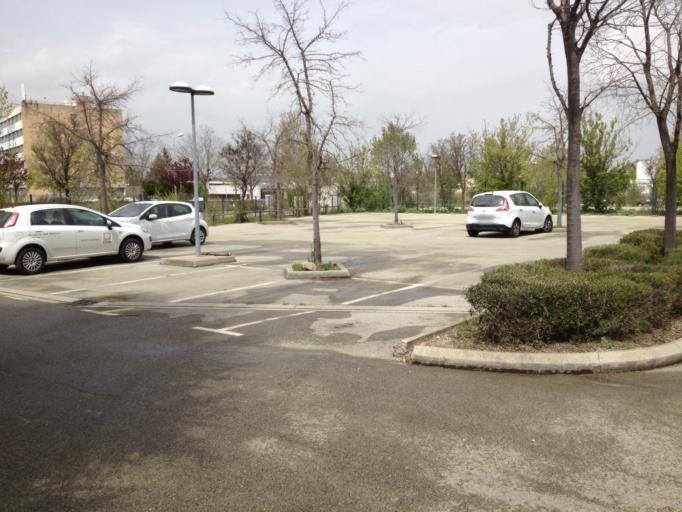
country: FR
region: Provence-Alpes-Cote d'Azur
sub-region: Departement des Bouches-du-Rhone
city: Cabries
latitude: 43.4920
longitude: 5.3739
